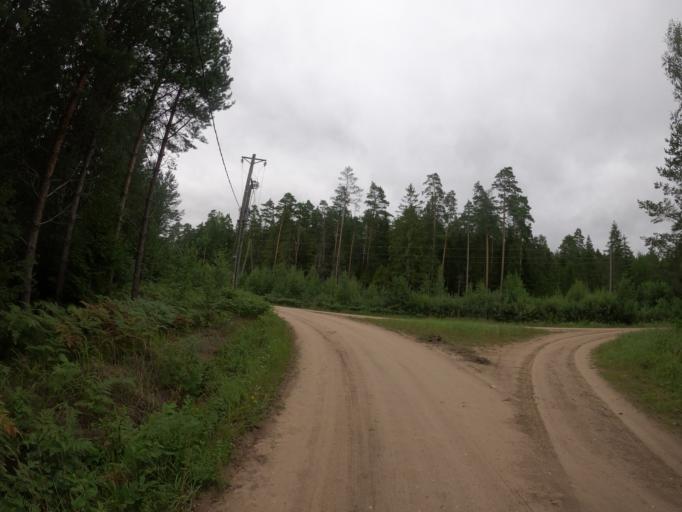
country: LV
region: Kuldigas Rajons
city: Kuldiga
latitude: 57.0218
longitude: 22.0069
